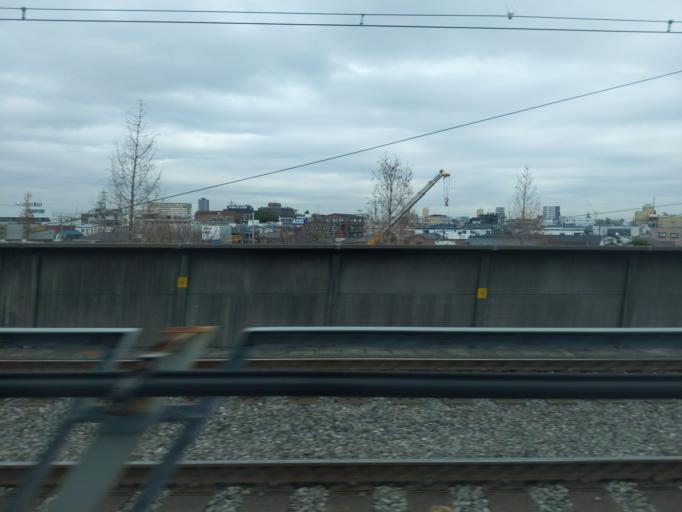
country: JP
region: Saitama
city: Shimotoda
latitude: 35.8146
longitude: 139.6713
